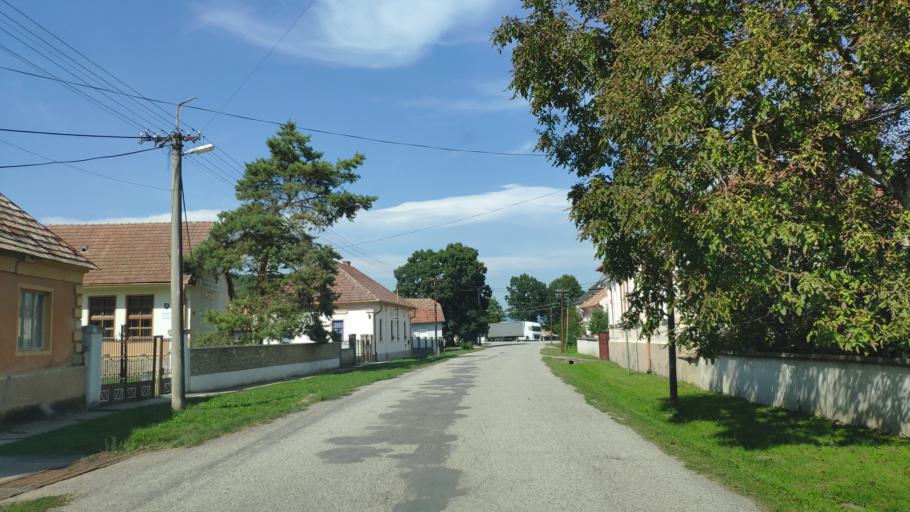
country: HU
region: Borsod-Abauj-Zemplen
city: Putnok
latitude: 48.4494
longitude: 20.3157
